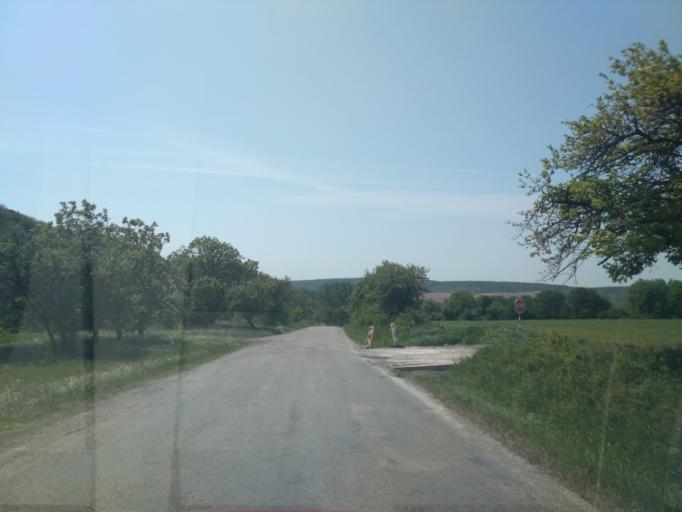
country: SK
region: Kosicky
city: Kosice
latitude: 48.7885
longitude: 21.3443
